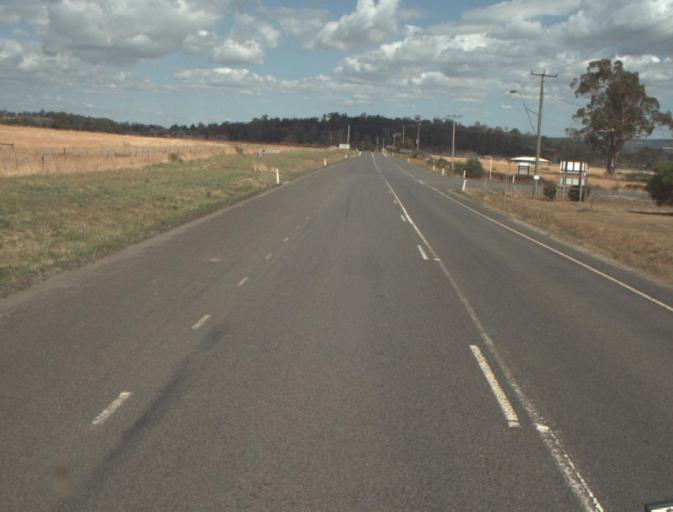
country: AU
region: Tasmania
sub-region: Launceston
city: Mayfield
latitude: -41.3092
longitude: 147.0508
